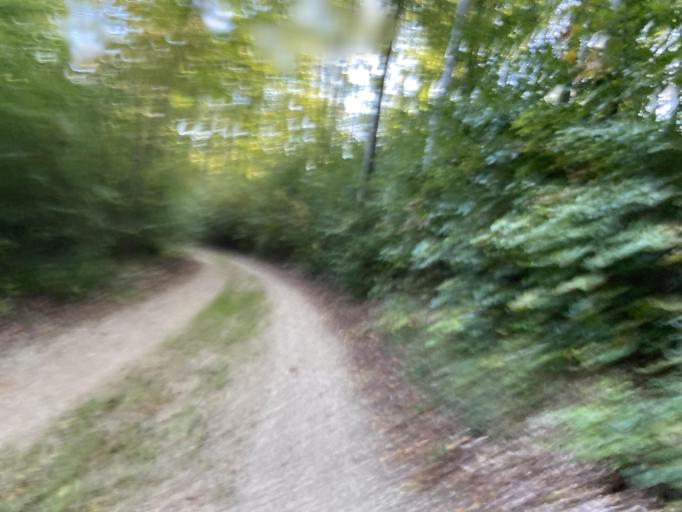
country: DE
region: Baden-Wuerttemberg
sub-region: Tuebingen Region
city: Bingen
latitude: 48.1338
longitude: 9.2744
